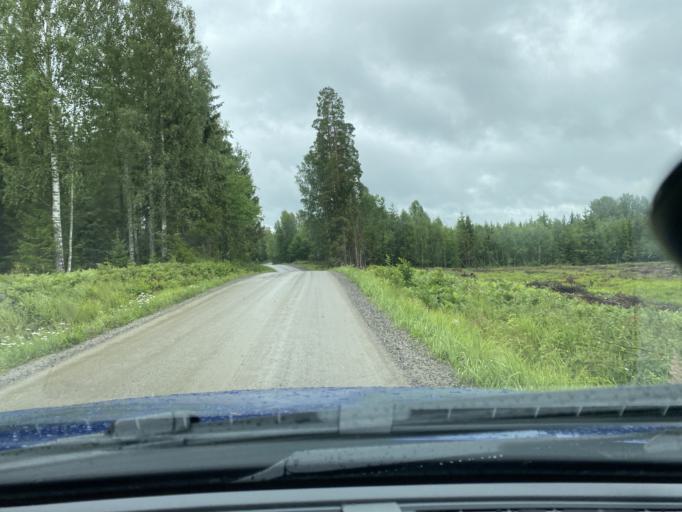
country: FI
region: Pirkanmaa
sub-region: Lounais-Pirkanmaa
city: Punkalaidun
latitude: 61.1477
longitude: 23.2614
